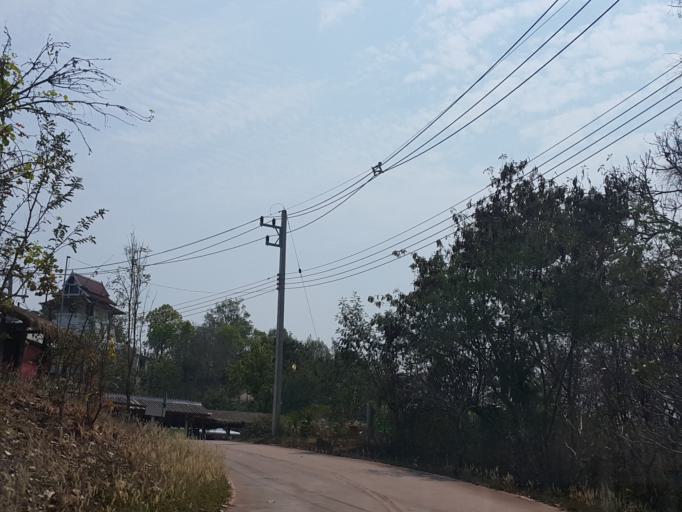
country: TH
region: Lampang
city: Chae Hom
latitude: 18.7441
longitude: 99.5427
